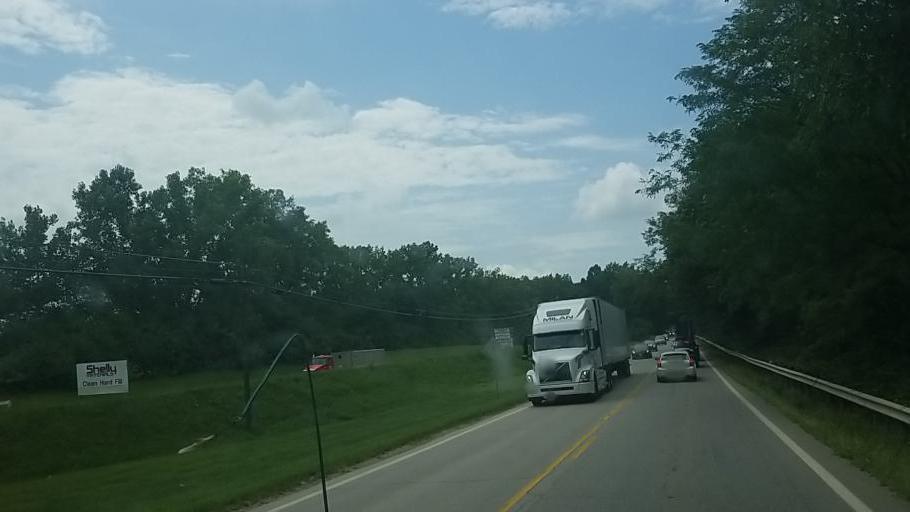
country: US
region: Ohio
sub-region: Franklin County
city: Obetz
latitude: 39.8326
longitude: -82.9869
